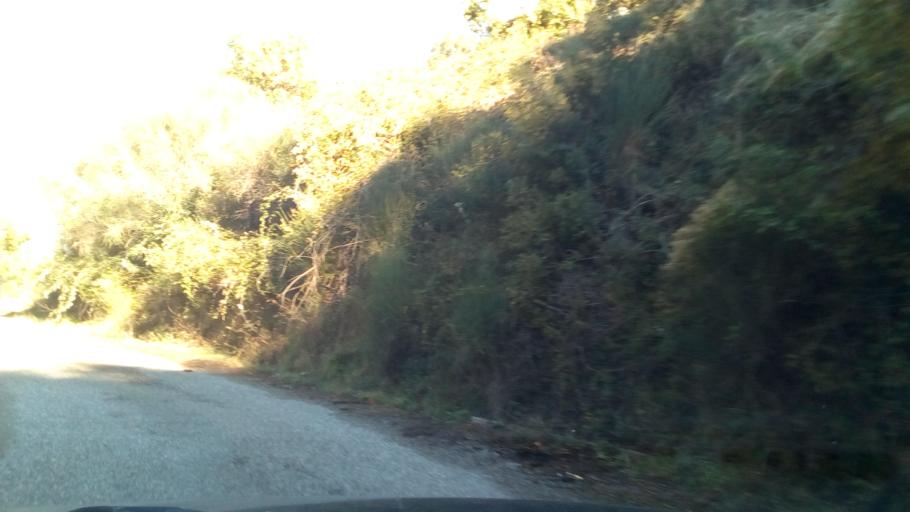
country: GR
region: West Greece
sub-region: Nomos Aitolias kai Akarnanias
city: Nafpaktos
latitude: 38.5617
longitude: 21.8527
